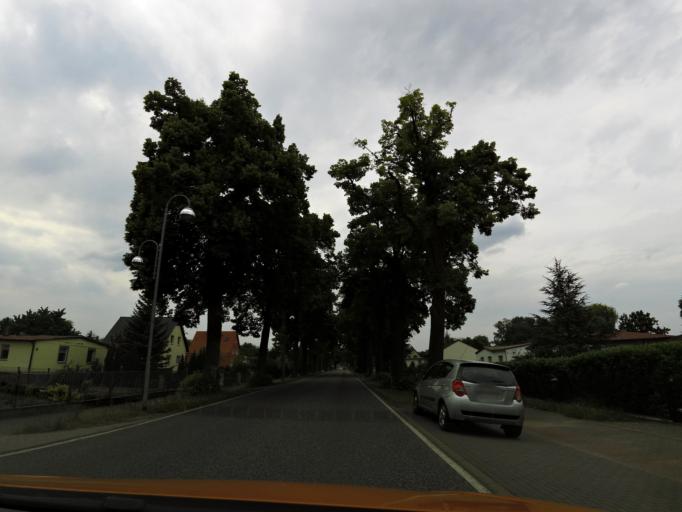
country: DE
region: Brandenburg
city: Zossen
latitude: 52.2081
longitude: 13.4553
